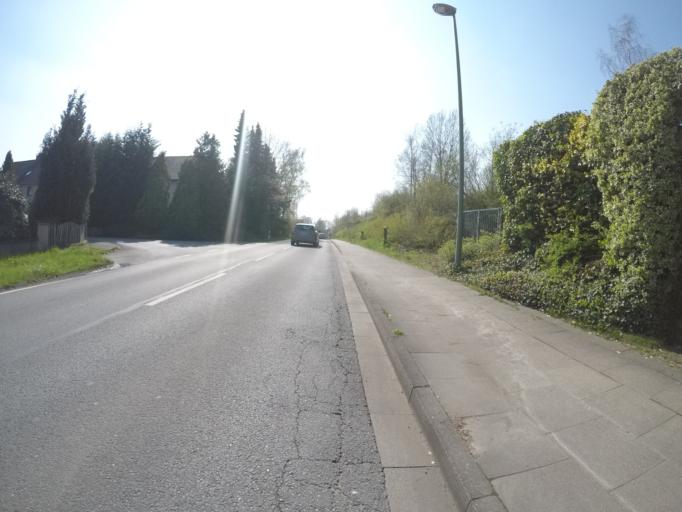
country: DE
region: North Rhine-Westphalia
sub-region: Regierungsbezirk Detmold
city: Herford
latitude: 52.0798
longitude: 8.6072
